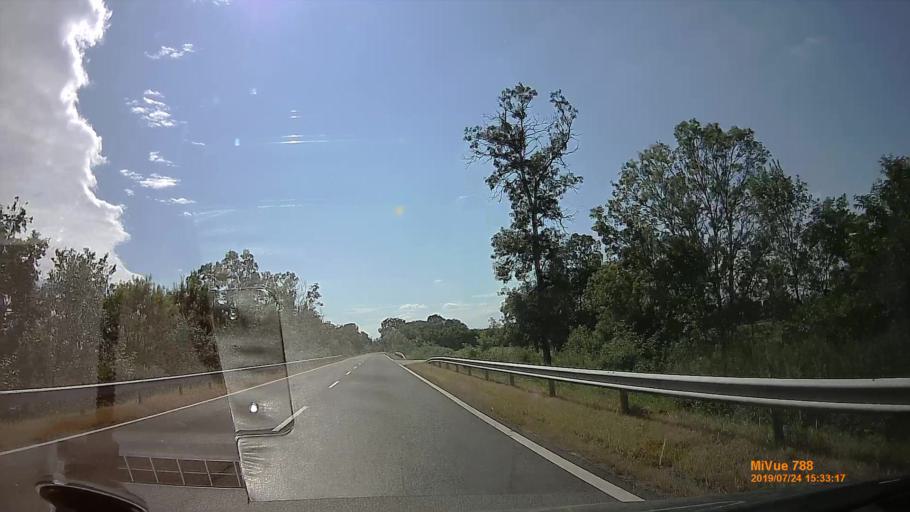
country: HU
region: Szabolcs-Szatmar-Bereg
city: Vasarosnameny
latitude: 48.1512
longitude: 22.3994
